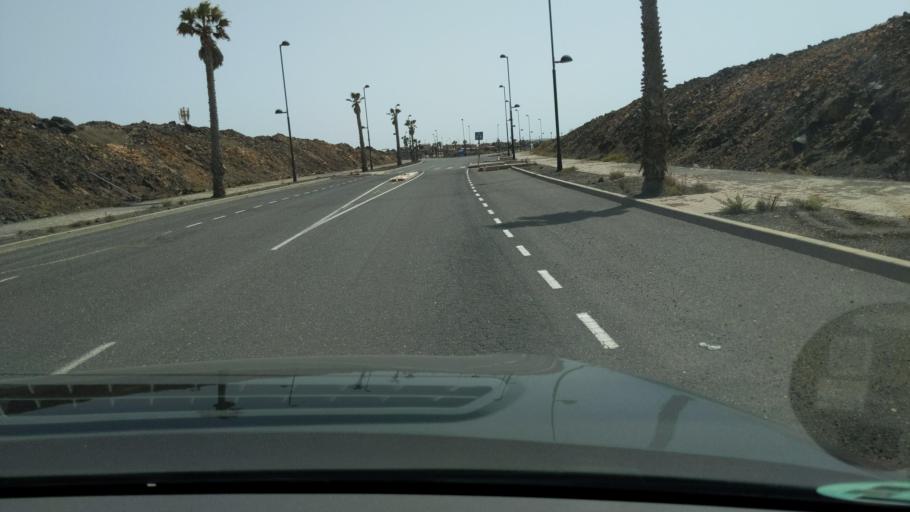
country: ES
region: Canary Islands
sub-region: Provincia de Las Palmas
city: Corralejo
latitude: 28.7357
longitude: -13.9450
